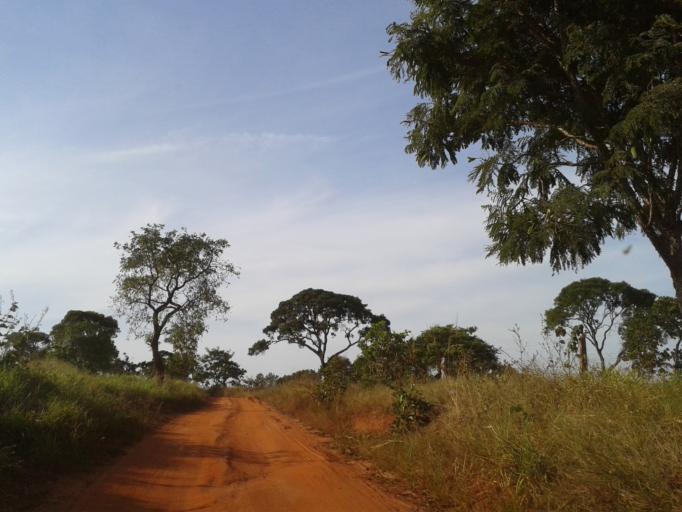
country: BR
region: Minas Gerais
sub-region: Campina Verde
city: Campina Verde
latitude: -19.5242
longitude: -49.6139
